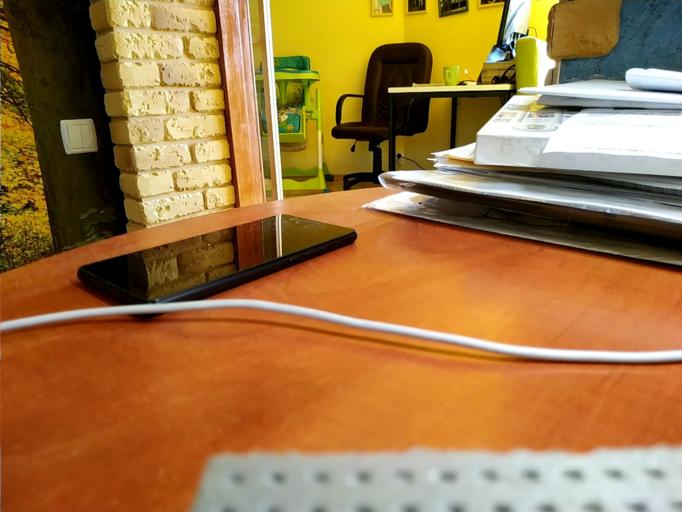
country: RU
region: Tverskaya
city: Kalashnikovo
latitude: 57.3892
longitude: 35.2995
